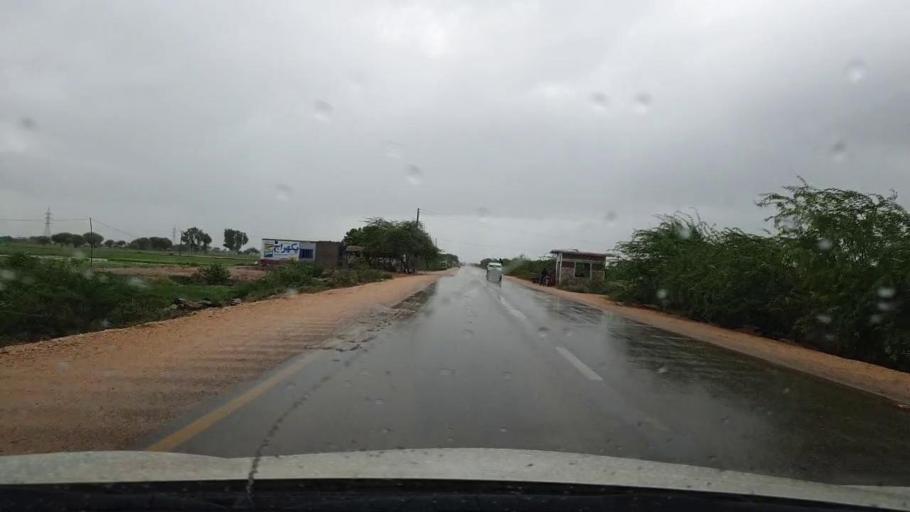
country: PK
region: Sindh
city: Kario
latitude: 24.6534
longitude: 68.5775
